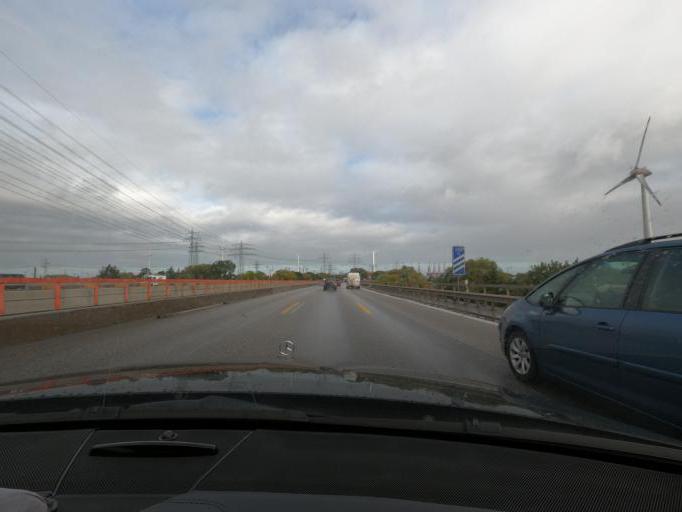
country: DE
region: Hamburg
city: Altona
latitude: 53.5077
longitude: 9.9125
